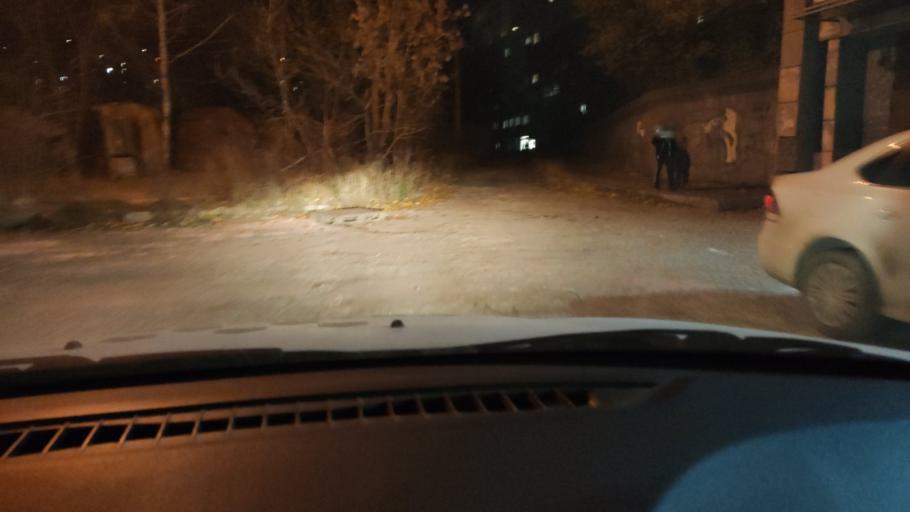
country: RU
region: Perm
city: Perm
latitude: 57.9816
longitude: 56.2849
